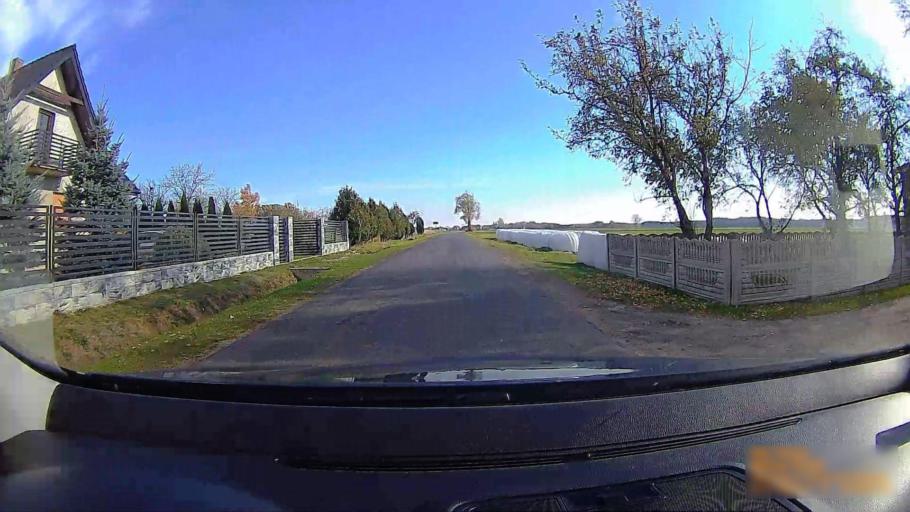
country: PL
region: Greater Poland Voivodeship
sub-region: Powiat ostrzeszowski
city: Doruchow
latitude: 51.3951
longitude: 18.0360
